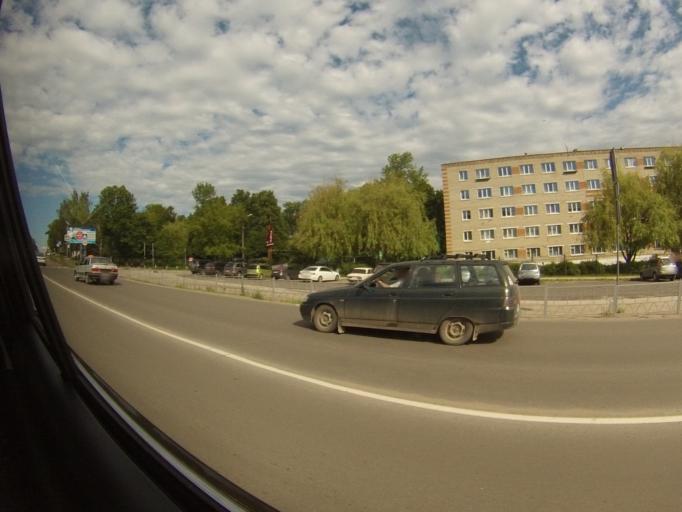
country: RU
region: Orjol
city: Mtsensk
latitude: 53.2882
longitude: 36.5923
